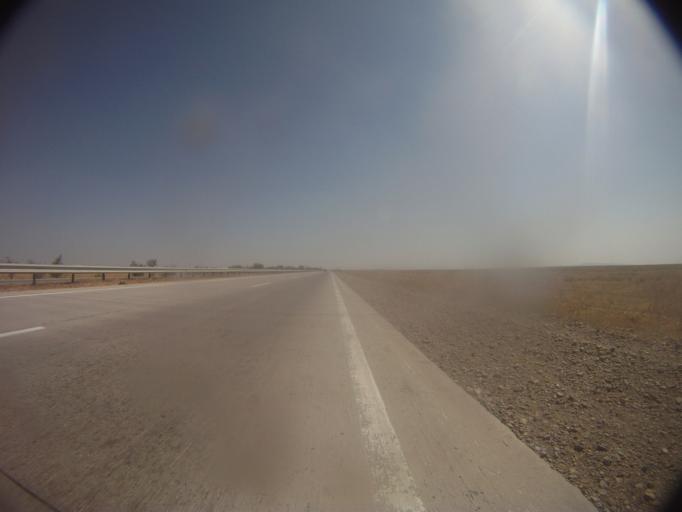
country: KZ
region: Zhambyl
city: Taraz
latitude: 42.7913
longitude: 71.0693
